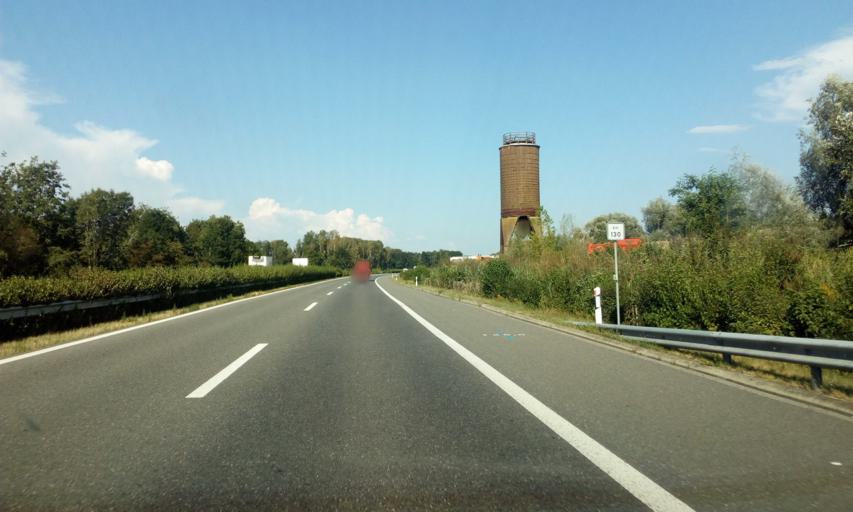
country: CH
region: Vaud
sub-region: Broye-Vully District
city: Avenches
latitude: 46.8918
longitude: 7.0423
